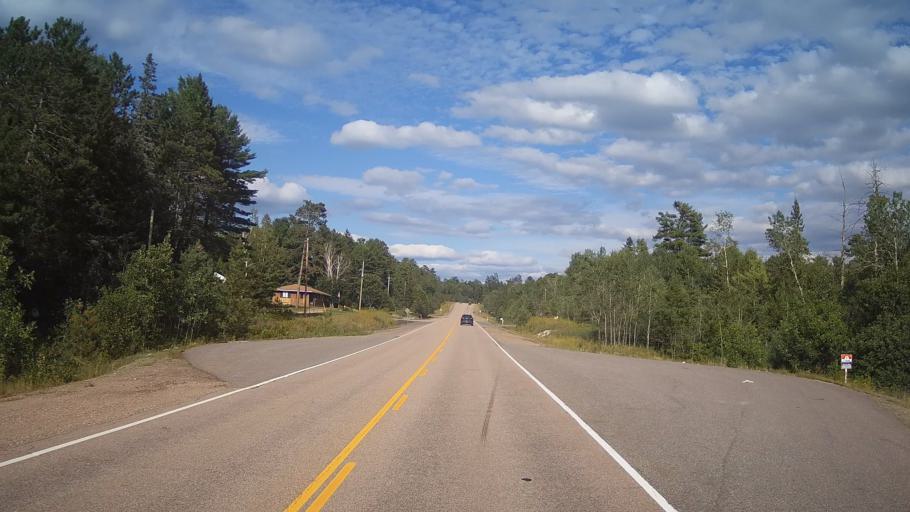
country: CA
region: Ontario
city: Mattawa
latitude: 46.2717
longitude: -78.9759
